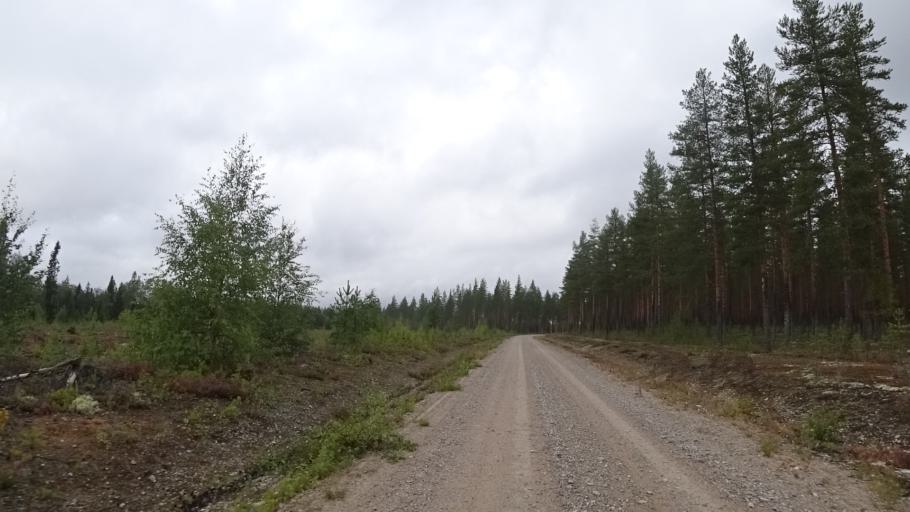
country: FI
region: North Karelia
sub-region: Pielisen Karjala
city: Lieksa
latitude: 63.5203
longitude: 30.1024
